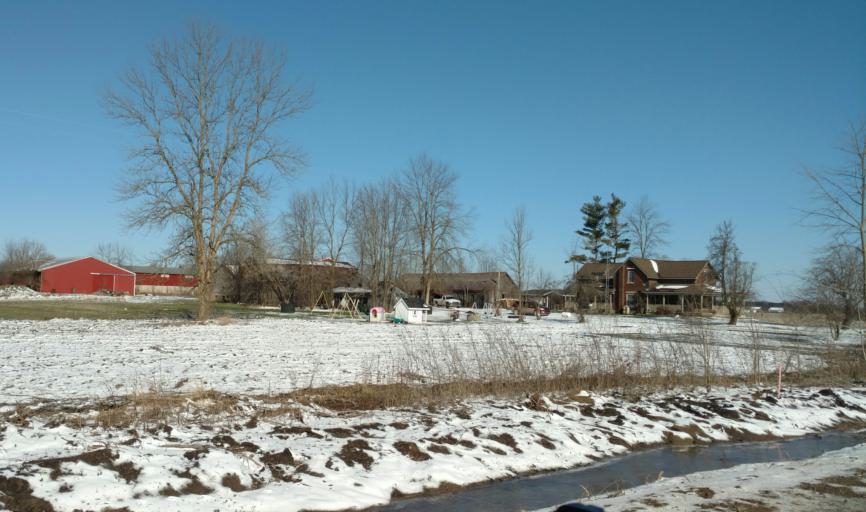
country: US
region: Michigan
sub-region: Gladwin County
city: Gladwin
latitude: 44.0394
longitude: -84.4674
